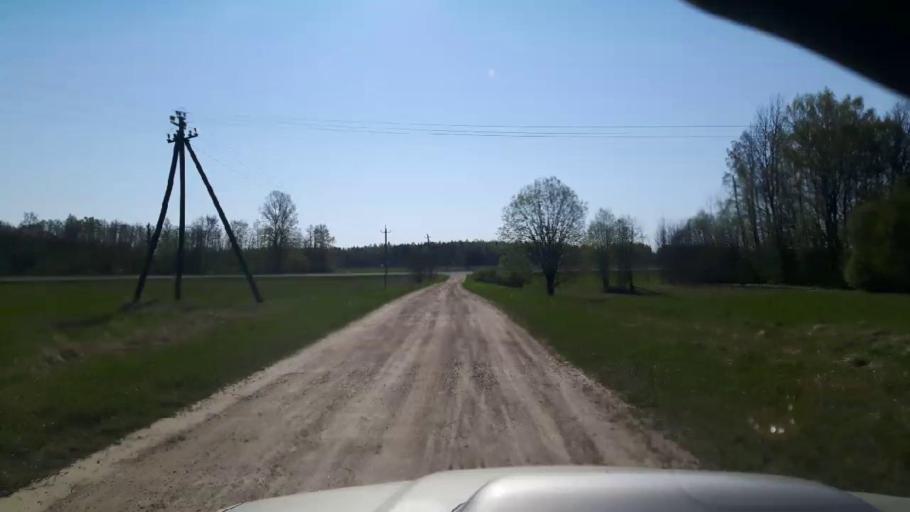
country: EE
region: Paernumaa
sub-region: Sindi linn
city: Sindi
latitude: 58.4528
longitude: 24.7760
